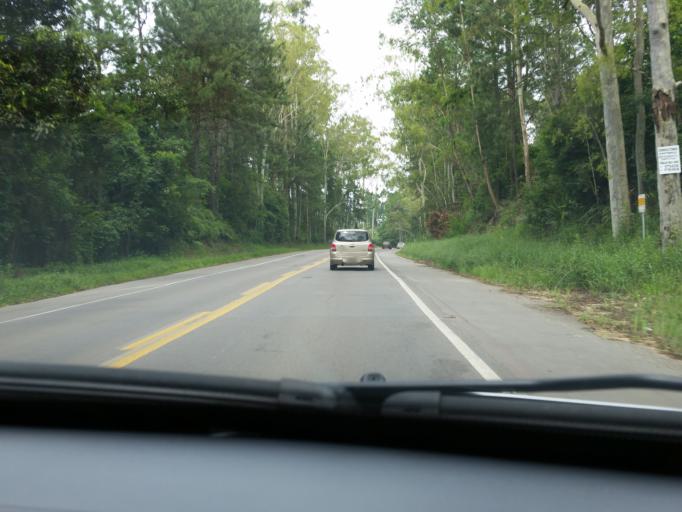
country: BR
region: Santa Catarina
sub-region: Rio Do Sul
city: Rio do Sul
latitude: -27.1700
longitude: -49.5738
